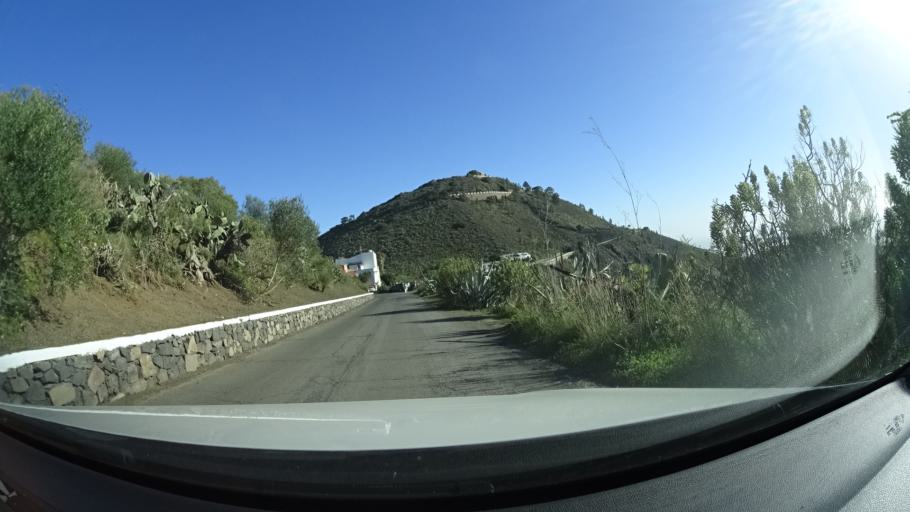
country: ES
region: Canary Islands
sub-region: Provincia de Las Palmas
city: Santa Brigida
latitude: 28.0334
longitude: -15.4610
